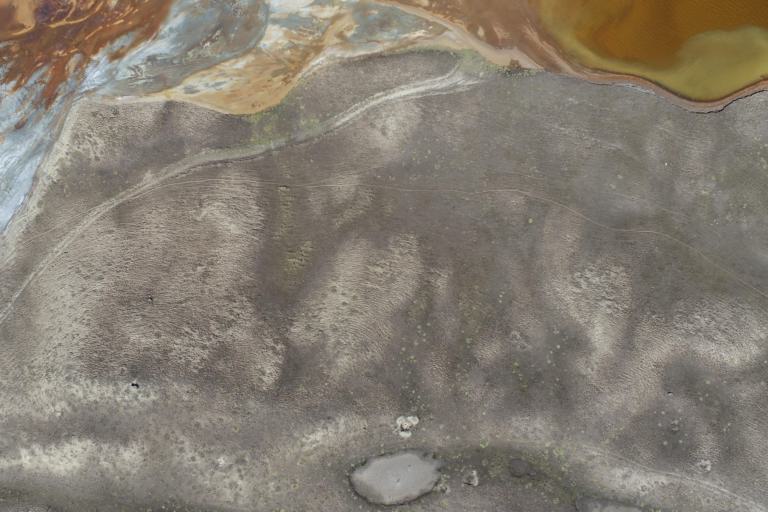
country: BO
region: La Paz
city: La Paz
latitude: -16.3450
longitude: -68.1598
